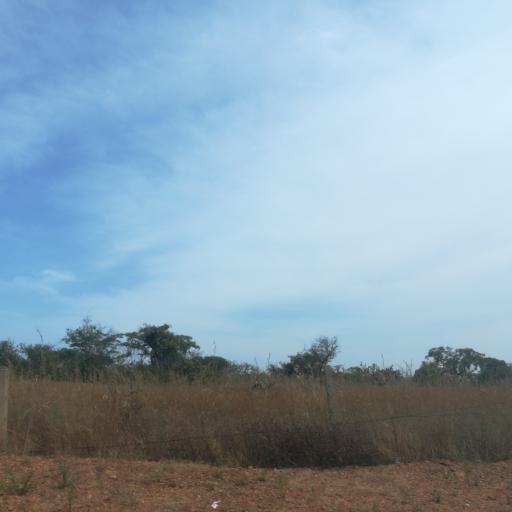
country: NG
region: Plateau
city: Jos
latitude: 9.8846
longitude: 8.8451
